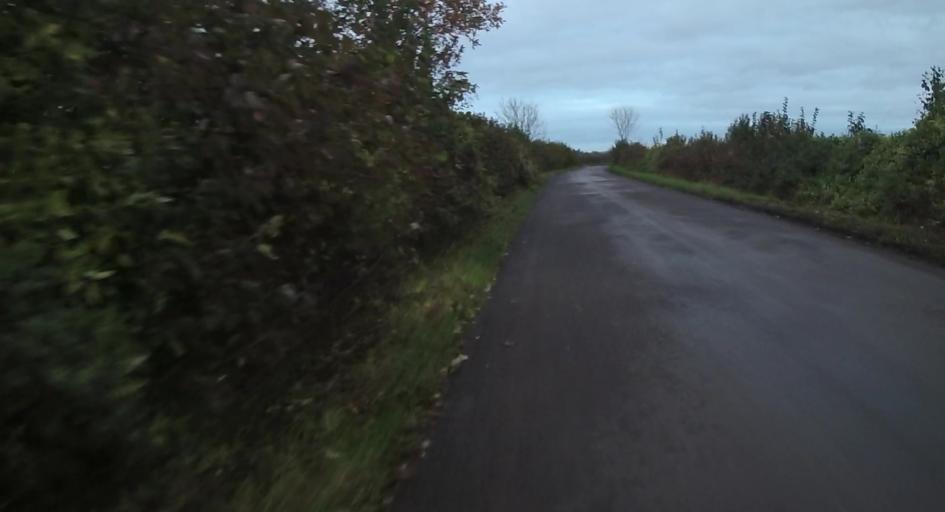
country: GB
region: England
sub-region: Hampshire
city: Long Sutton
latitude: 51.2229
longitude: -0.8801
